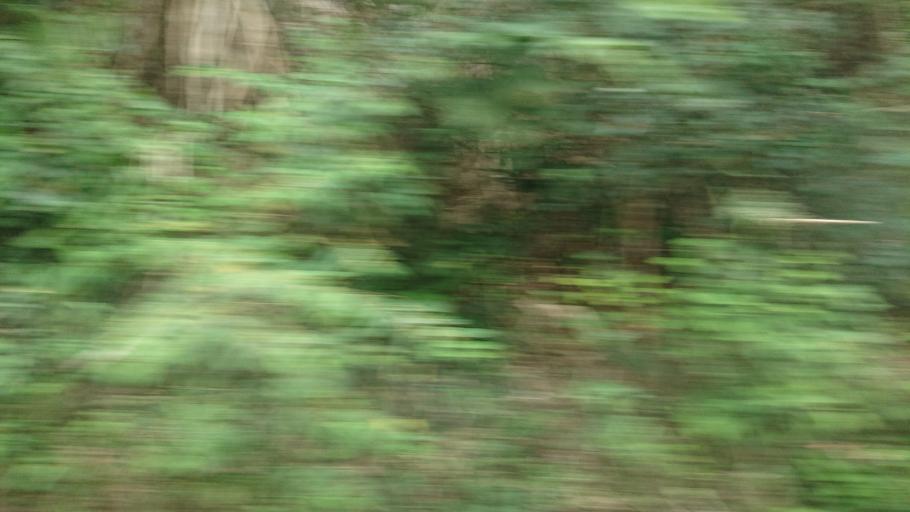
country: TW
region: Taiwan
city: Lugu
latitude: 23.5836
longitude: 120.6956
